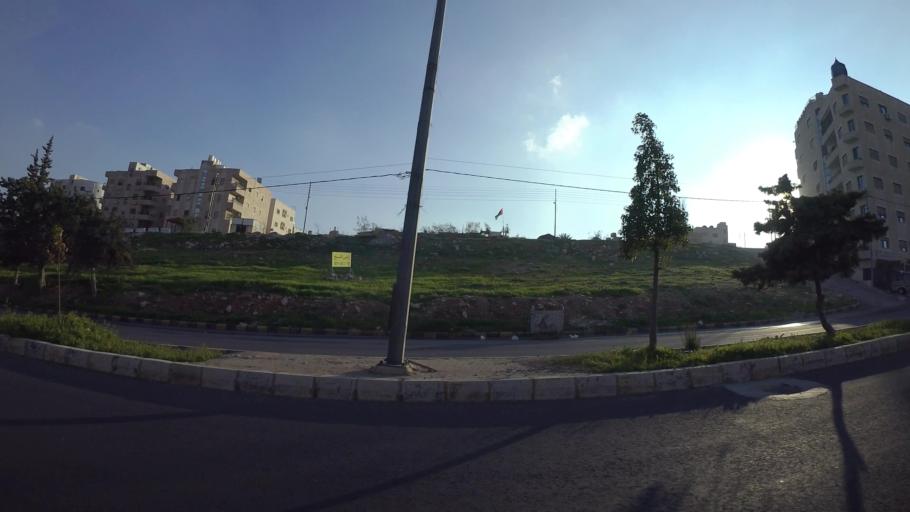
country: JO
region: Amman
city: Amman
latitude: 31.9846
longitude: 35.9551
